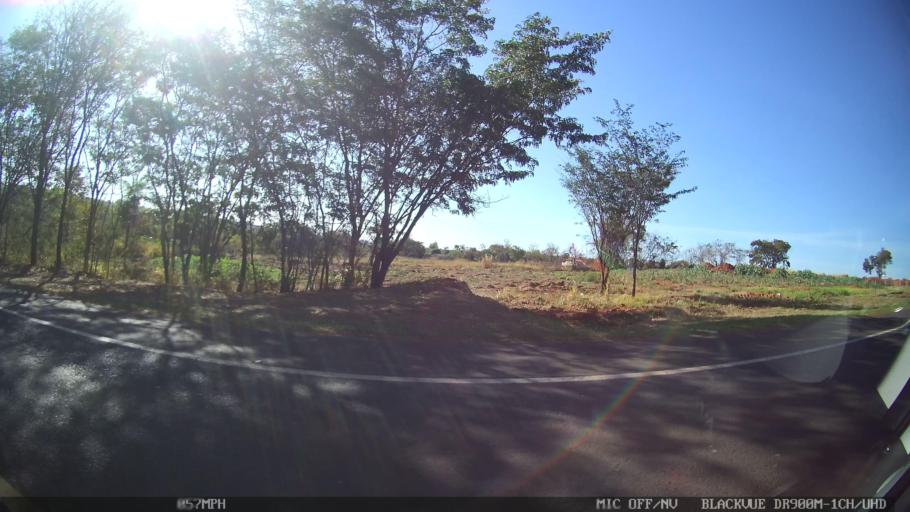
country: BR
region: Sao Paulo
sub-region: Olimpia
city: Olimpia
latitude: -20.7378
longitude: -48.8832
